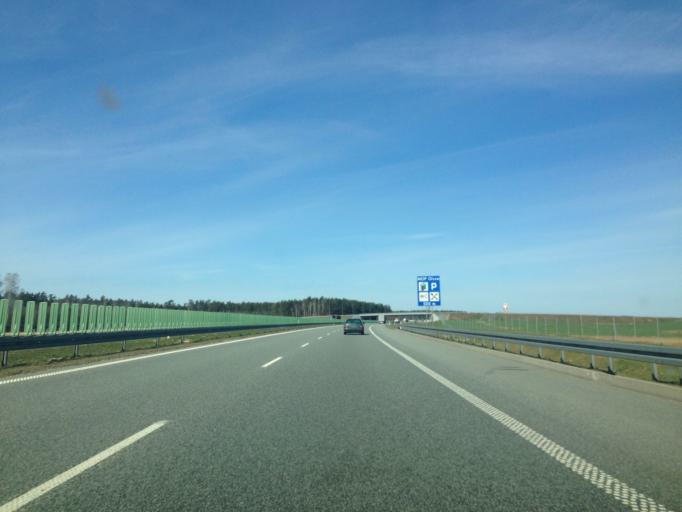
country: PL
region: Pomeranian Voivodeship
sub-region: Powiat starogardzki
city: Bobowo
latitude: 53.8788
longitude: 18.6273
